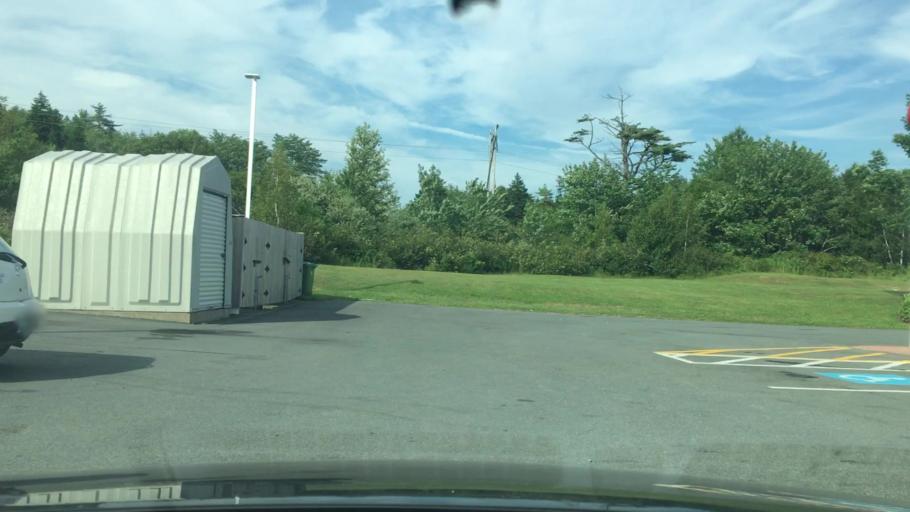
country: CA
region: Nova Scotia
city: Dartmouth
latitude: 44.7051
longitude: -63.8560
